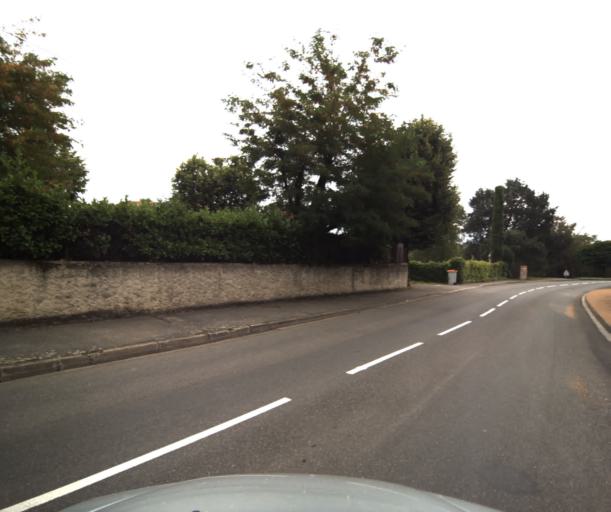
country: FR
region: Midi-Pyrenees
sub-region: Departement de la Haute-Garonne
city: Muret
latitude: 43.4619
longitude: 1.3311
